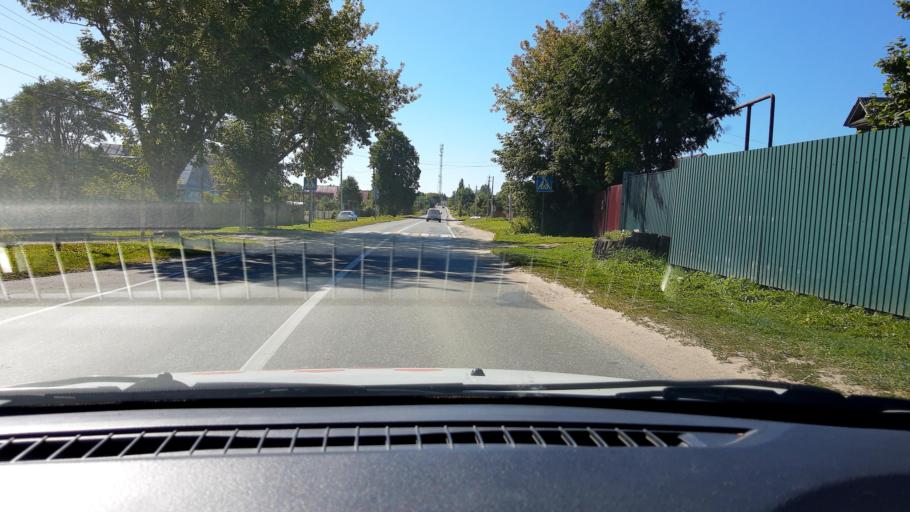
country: RU
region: Nizjnij Novgorod
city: Zavolzh'ye
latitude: 56.7226
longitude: 43.4139
